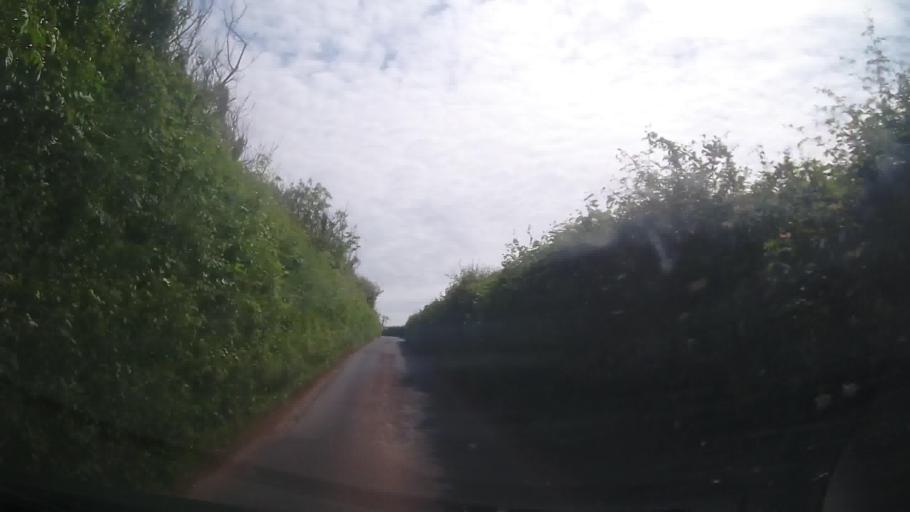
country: GB
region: England
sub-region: Devon
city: Salcombe
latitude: 50.2658
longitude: -3.6770
